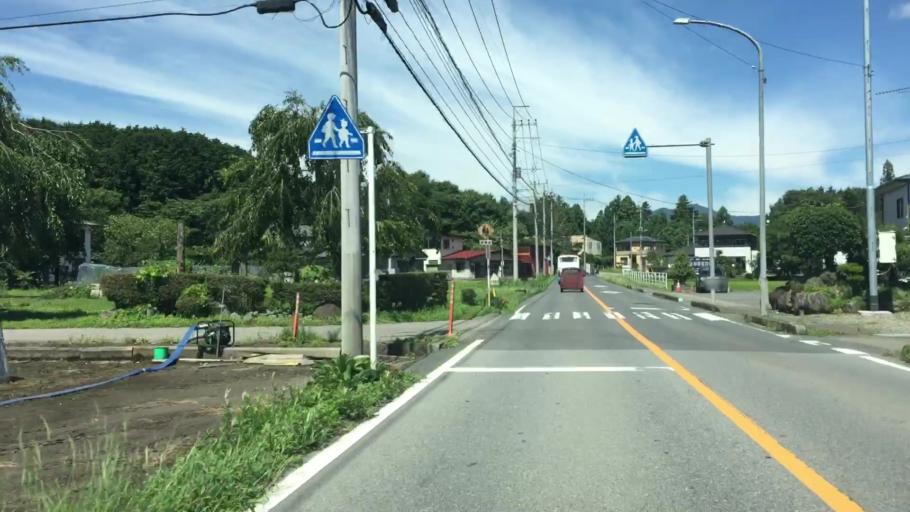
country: JP
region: Tochigi
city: Imaichi
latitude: 36.7454
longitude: 139.7382
